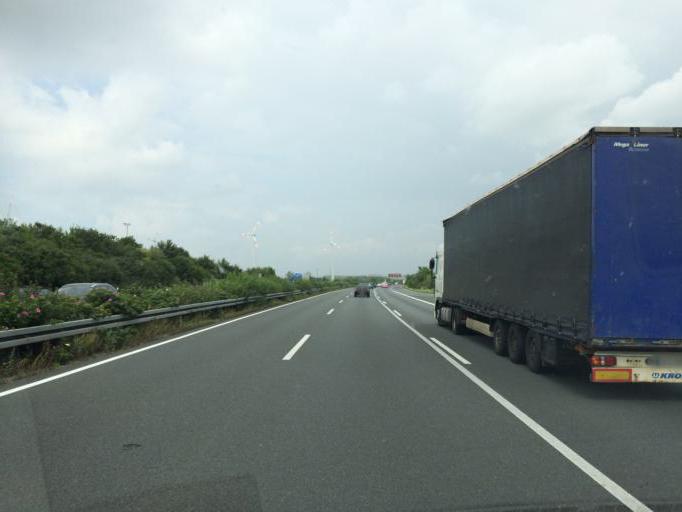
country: DE
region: Lower Saxony
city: Bad Nenndorf
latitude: 52.3471
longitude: 9.4221
